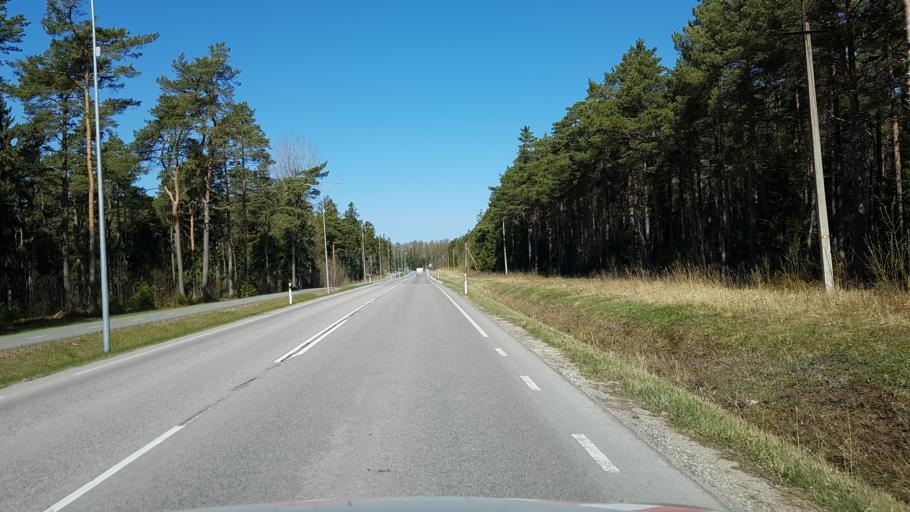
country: EE
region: Harju
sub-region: Viimsi vald
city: Viimsi
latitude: 59.5179
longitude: 24.8991
